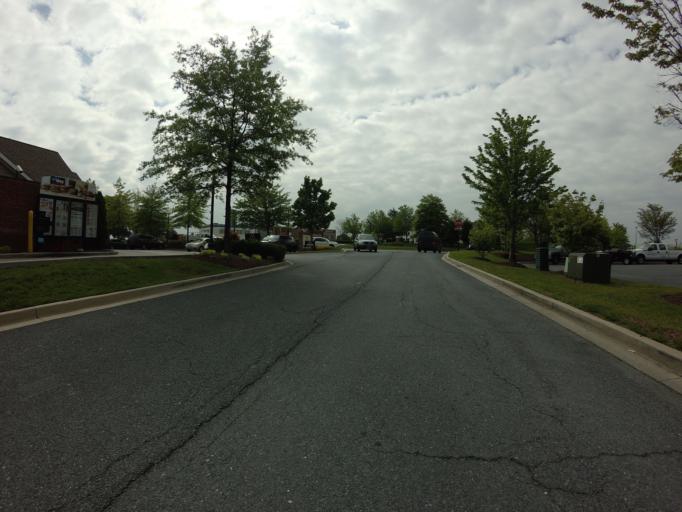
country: US
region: Maryland
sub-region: Frederick County
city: Urbana
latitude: 39.3254
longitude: -77.3499
